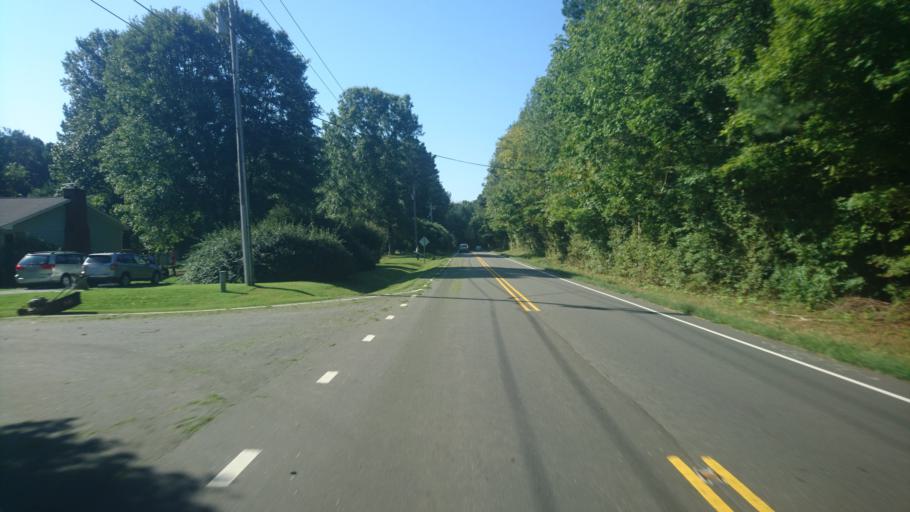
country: US
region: North Carolina
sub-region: Orange County
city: Hillsborough
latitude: 36.0050
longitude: -79.0659
